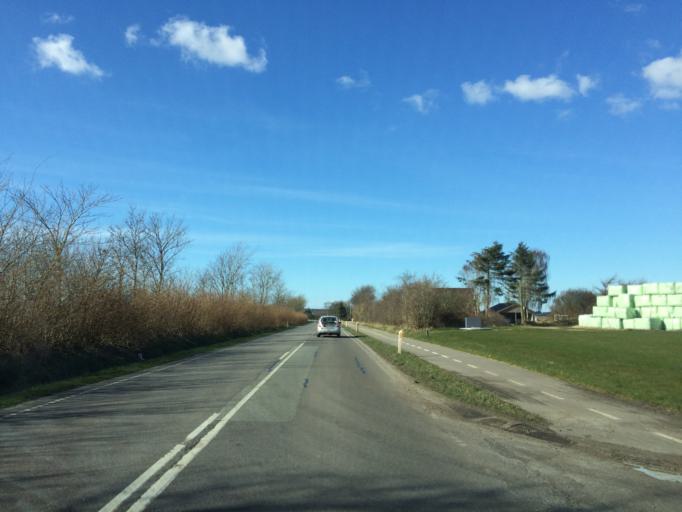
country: DK
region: South Denmark
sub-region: Varde Kommune
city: Oksbol
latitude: 55.7188
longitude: 8.2928
